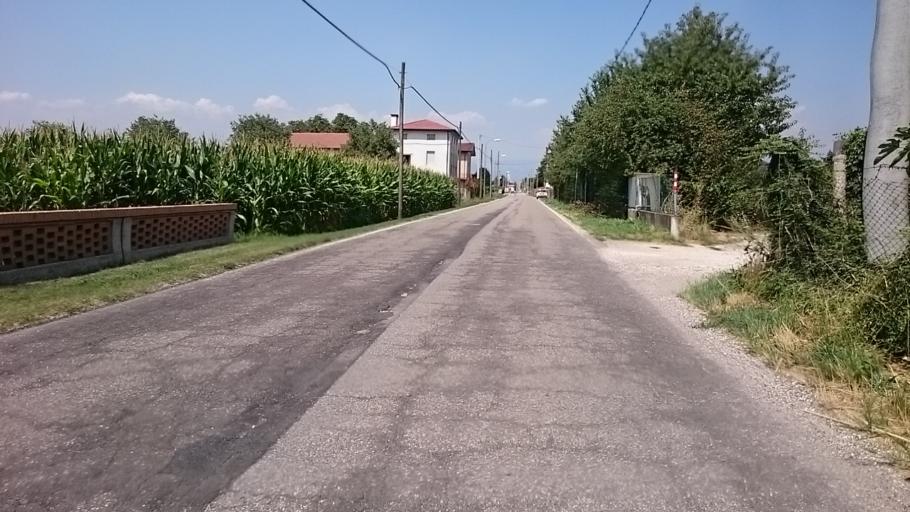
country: IT
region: Veneto
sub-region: Provincia di Padova
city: Fontaniva
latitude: 45.6554
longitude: 11.7582
